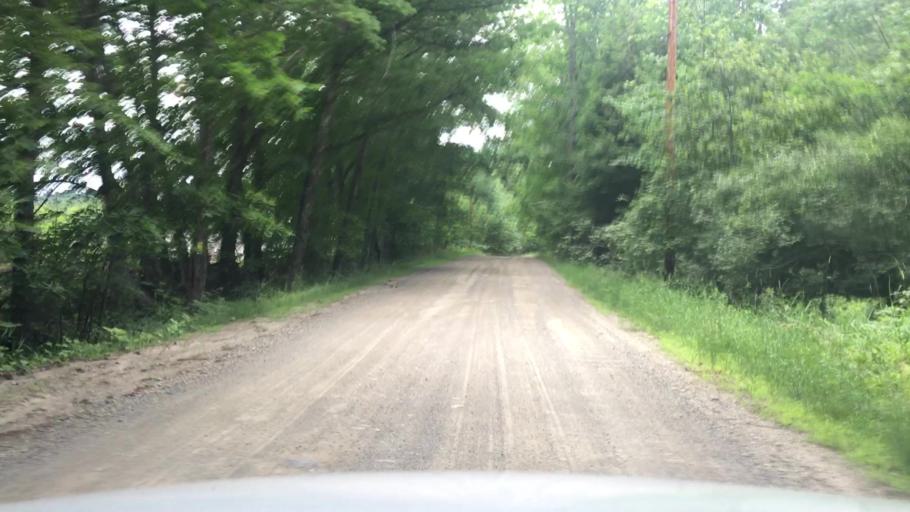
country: US
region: Maine
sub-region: Waldo County
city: Searsmont
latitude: 44.4270
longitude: -69.2563
